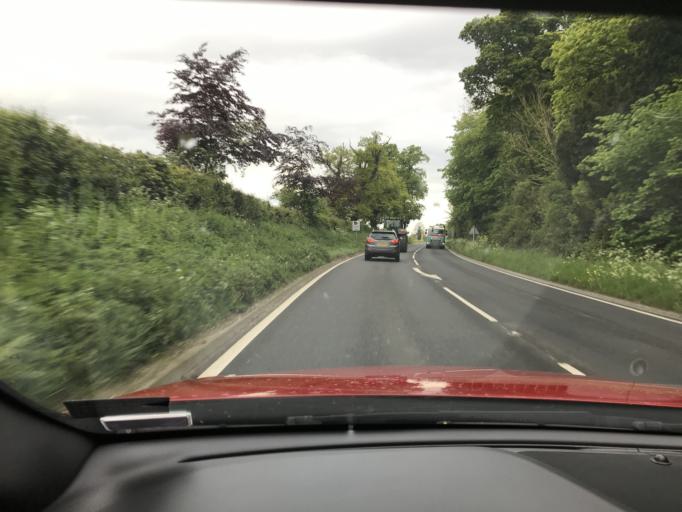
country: GB
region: England
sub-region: East Riding of Yorkshire
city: Cherry Burton
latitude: 53.8458
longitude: -0.5047
